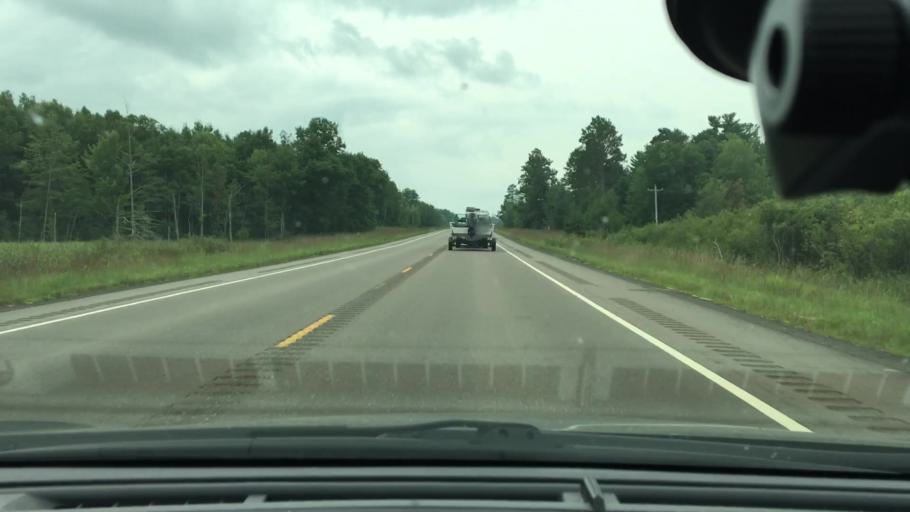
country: US
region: Minnesota
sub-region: Crow Wing County
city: Crosby
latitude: 46.5912
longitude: -93.9527
